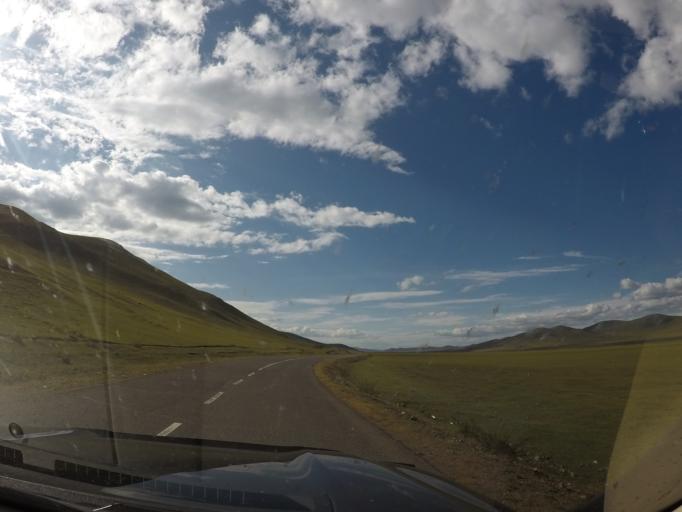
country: MN
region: Hentiy
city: Modot
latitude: 47.6774
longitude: 109.1153
